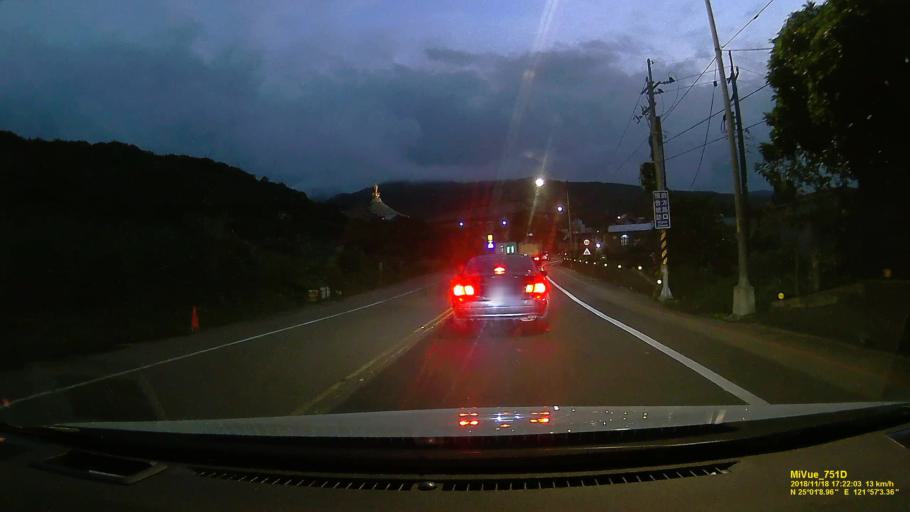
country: TW
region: Taiwan
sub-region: Keelung
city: Keelung
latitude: 25.0191
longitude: 121.9509
